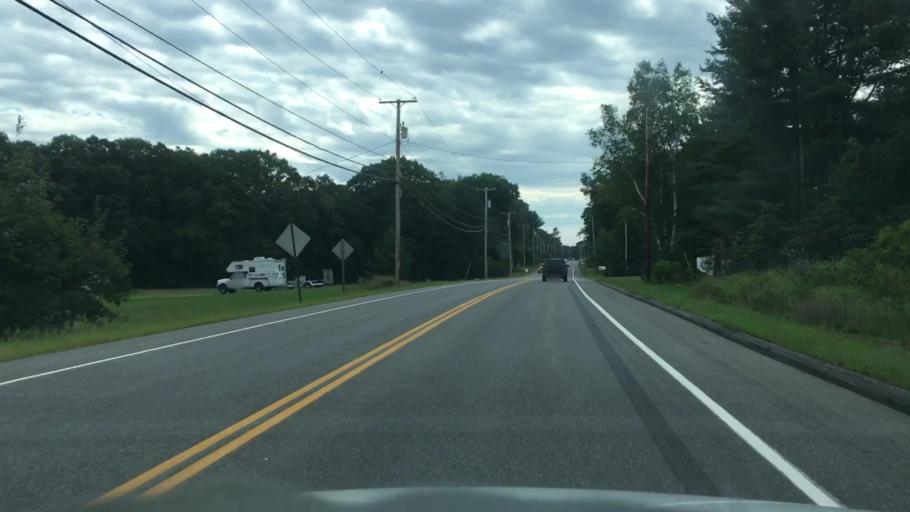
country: US
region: Maine
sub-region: York County
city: Wells Beach Station
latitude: 43.3311
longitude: -70.6242
